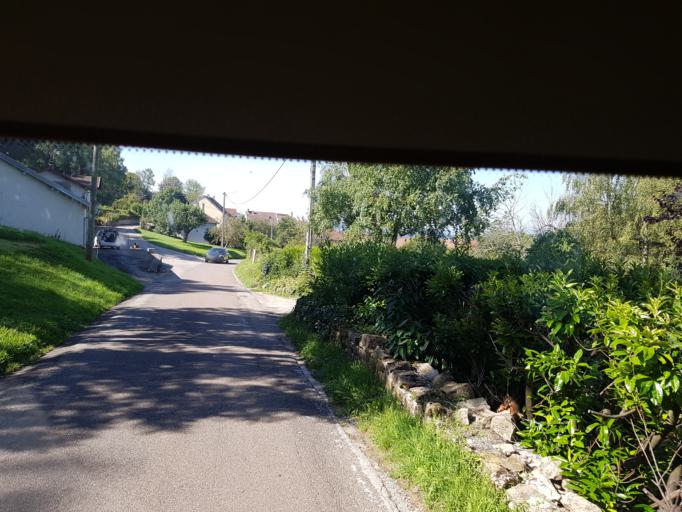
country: FR
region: Franche-Comte
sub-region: Departement du Jura
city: Perrigny
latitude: 46.6986
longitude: 5.6011
